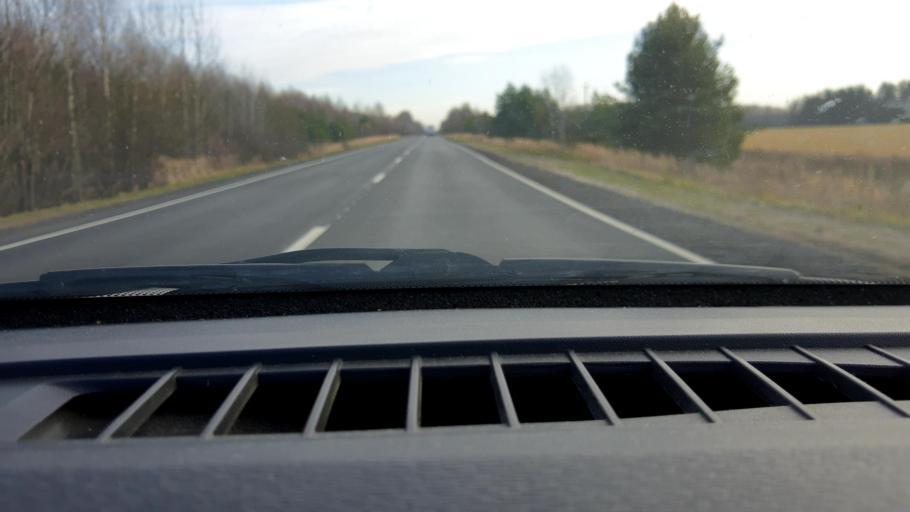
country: RU
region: Nizjnij Novgorod
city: Novaya Balakhna
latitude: 56.5941
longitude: 43.6518
